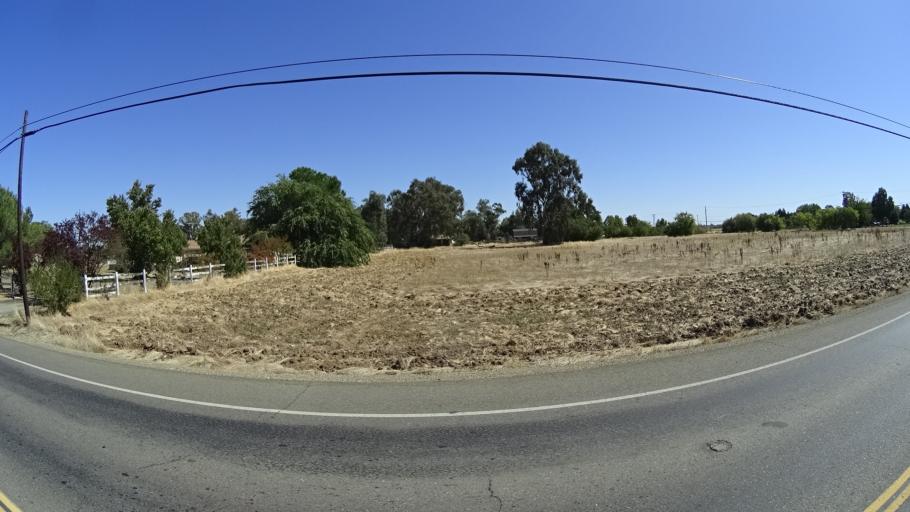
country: US
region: California
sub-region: Sacramento County
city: Elk Grove
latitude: 38.4101
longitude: -121.3346
